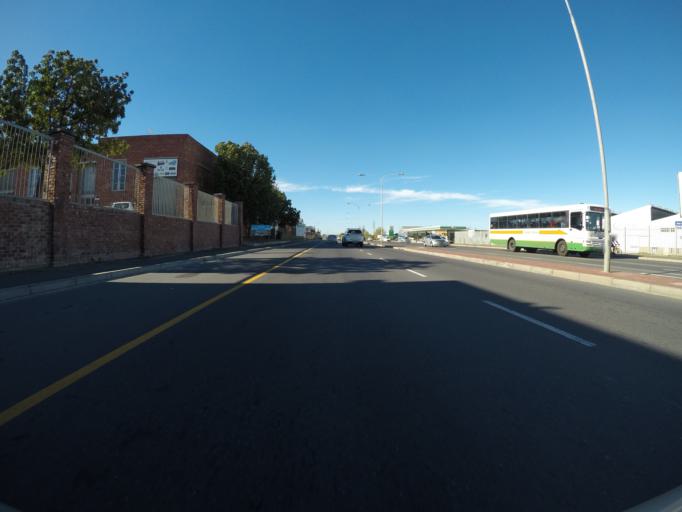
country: ZA
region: Western Cape
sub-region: City of Cape Town
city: Kraaifontein
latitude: -33.8990
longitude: 18.6705
